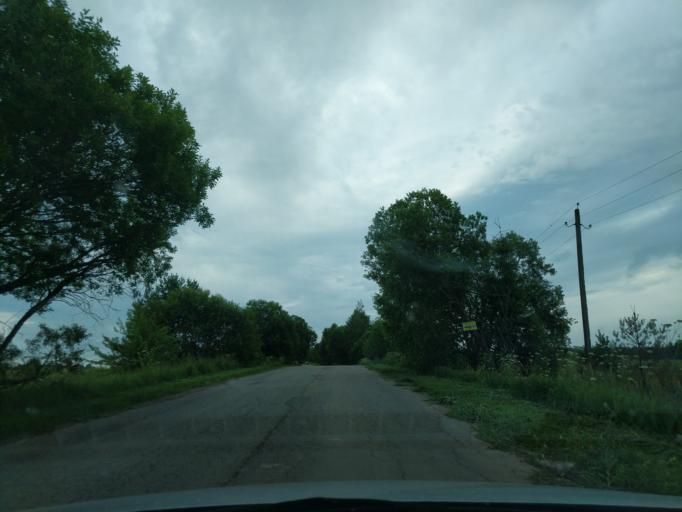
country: RU
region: Kaluga
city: Myatlevo
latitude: 54.7795
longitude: 35.7262
